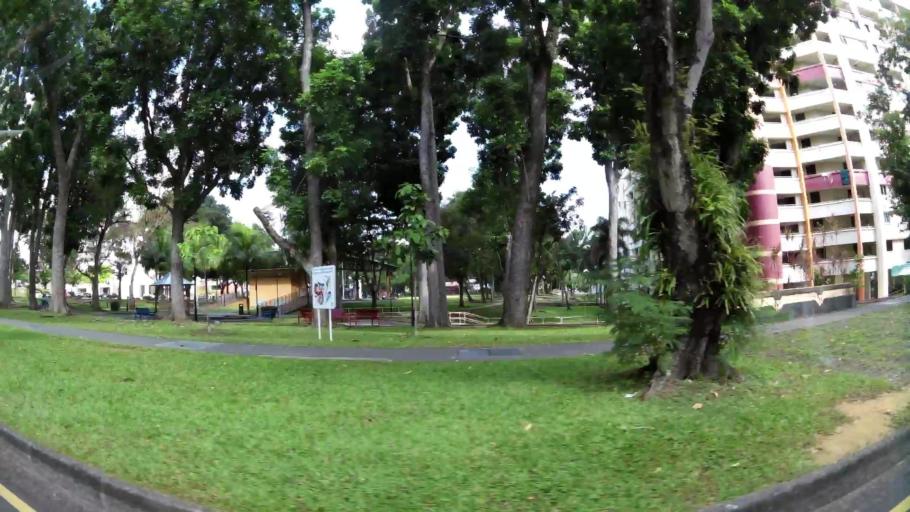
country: SG
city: Singapore
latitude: 1.3519
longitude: 103.8855
